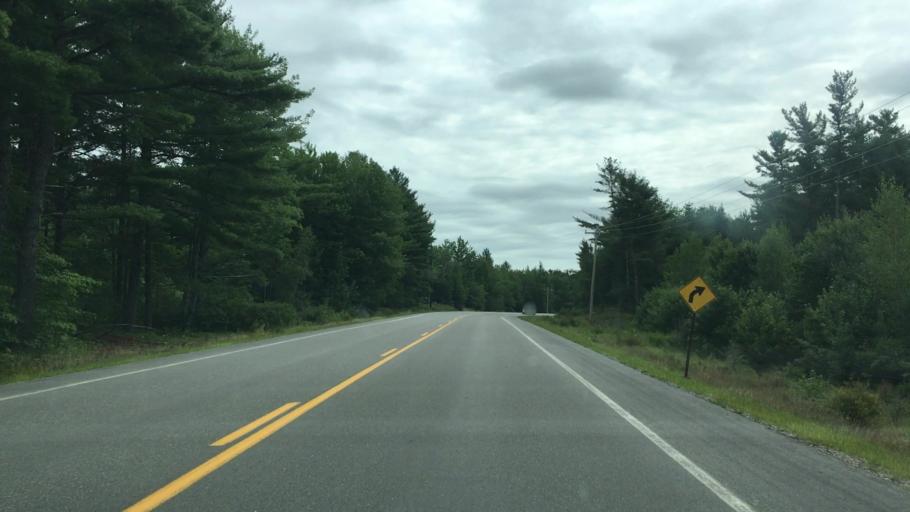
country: US
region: Maine
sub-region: Washington County
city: Machias
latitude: 45.0008
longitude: -67.5740
